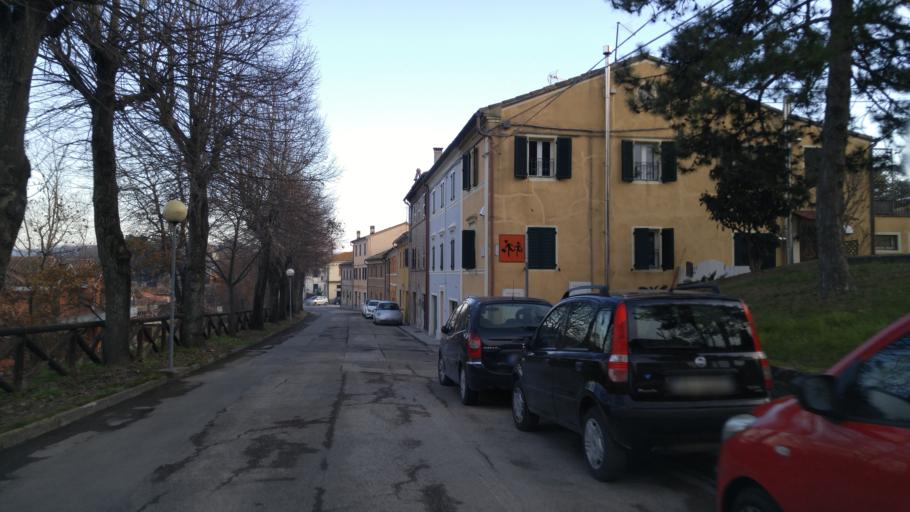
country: IT
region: The Marches
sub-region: Provincia di Pesaro e Urbino
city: Monte Porzio
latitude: 43.6926
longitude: 13.0421
